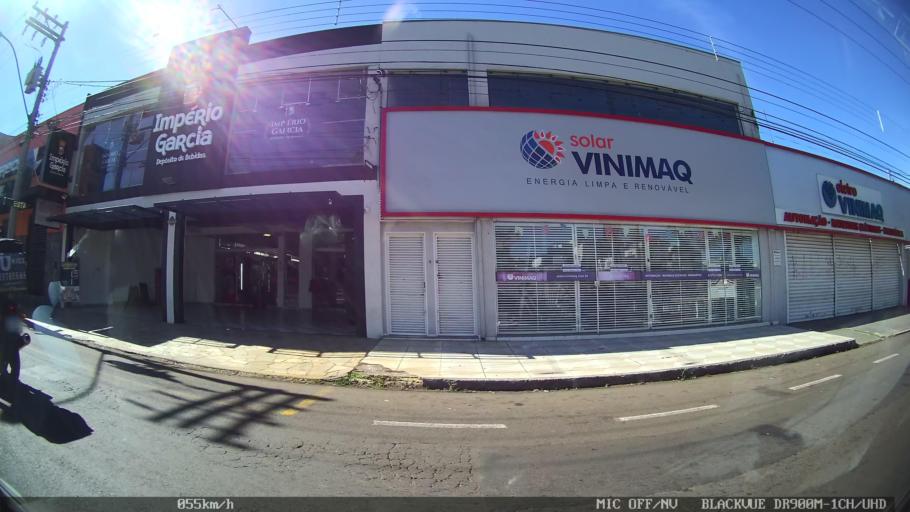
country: BR
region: Sao Paulo
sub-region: Franca
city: Franca
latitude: -20.5240
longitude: -47.4008
